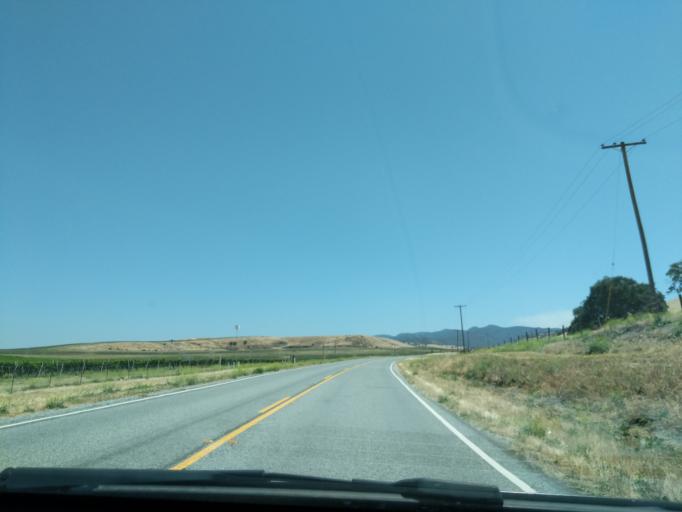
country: US
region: California
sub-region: Monterey County
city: King City
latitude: 36.1717
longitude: -121.1310
